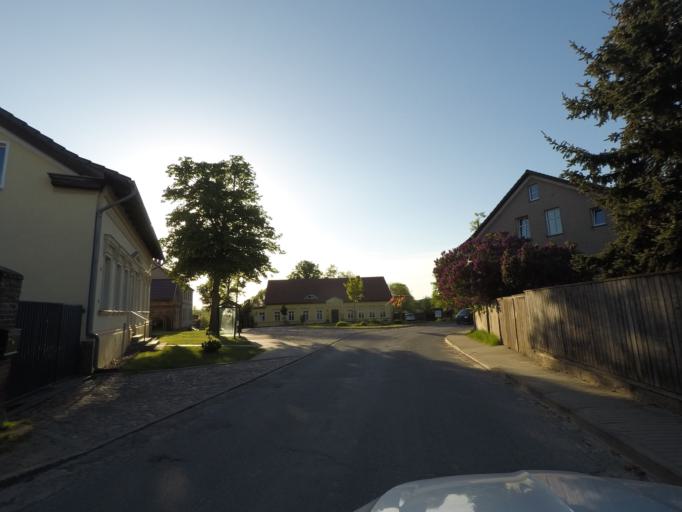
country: DE
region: Brandenburg
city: Liepe
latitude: 52.8335
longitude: 14.0050
